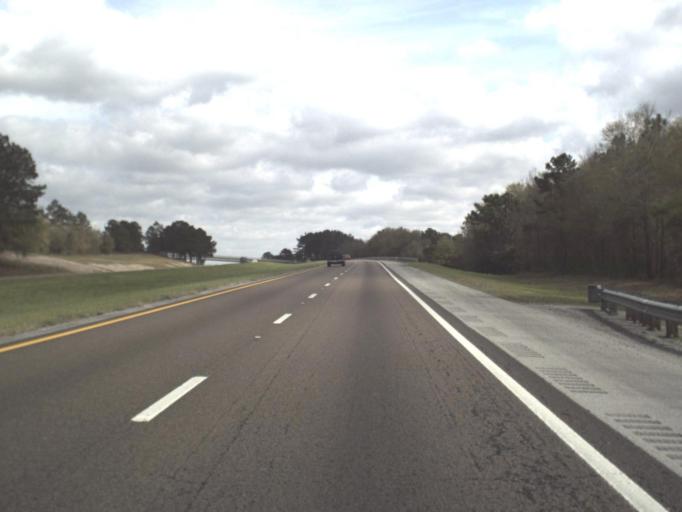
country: US
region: Florida
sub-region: Walton County
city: DeFuniak Springs
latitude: 30.7307
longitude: -86.2164
